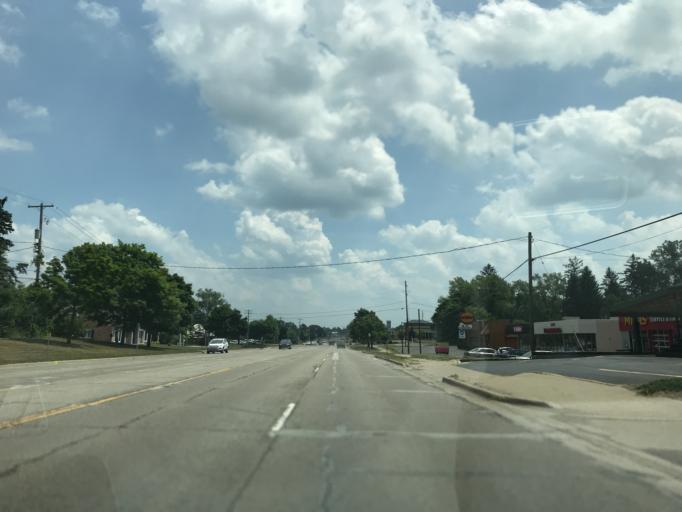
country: US
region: Michigan
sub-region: Ingham County
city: Okemos
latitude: 42.7229
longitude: -84.4325
